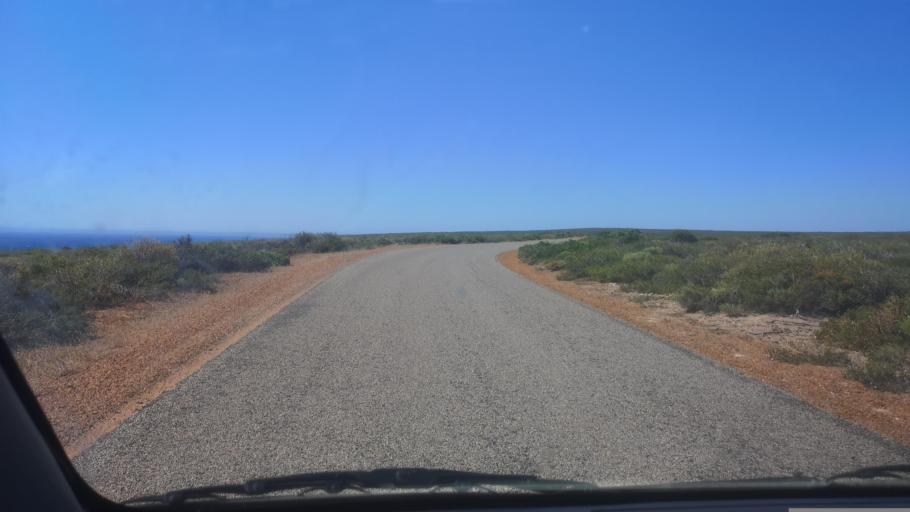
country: AU
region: Western Australia
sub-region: Northampton Shire
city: Kalbarri
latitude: -27.8180
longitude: 114.1170
